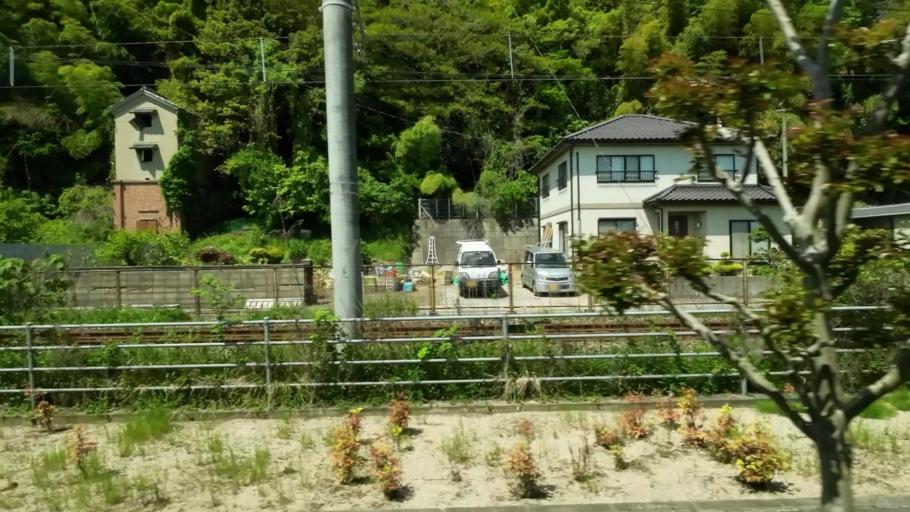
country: JP
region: Ehime
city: Hojo
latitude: 34.0786
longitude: 132.9852
